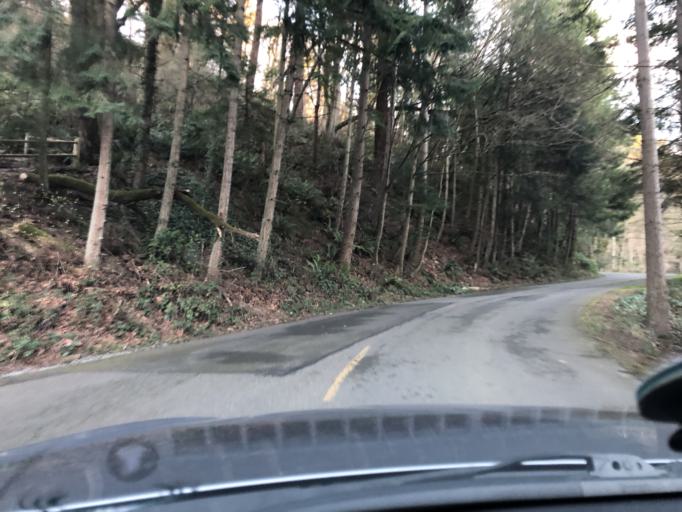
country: US
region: Washington
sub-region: Pierce County
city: Tacoma
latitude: 47.3198
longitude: -122.4134
